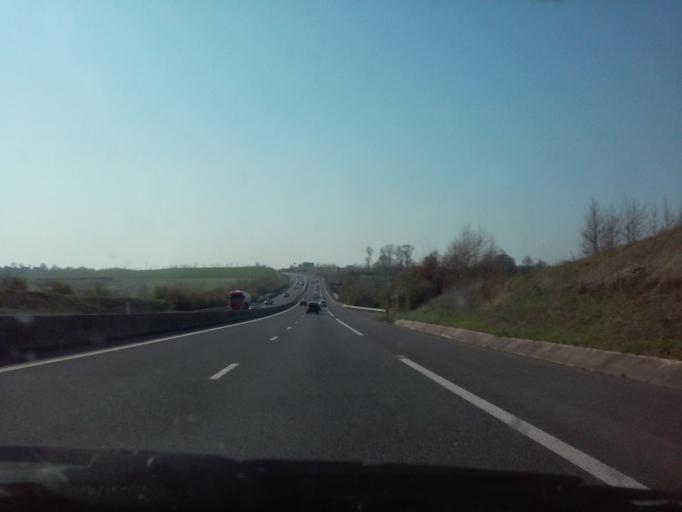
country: FR
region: Lower Normandy
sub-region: Departement du Calvados
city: Saint-Vigor-le-Grand
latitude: 49.2496
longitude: -0.6320
